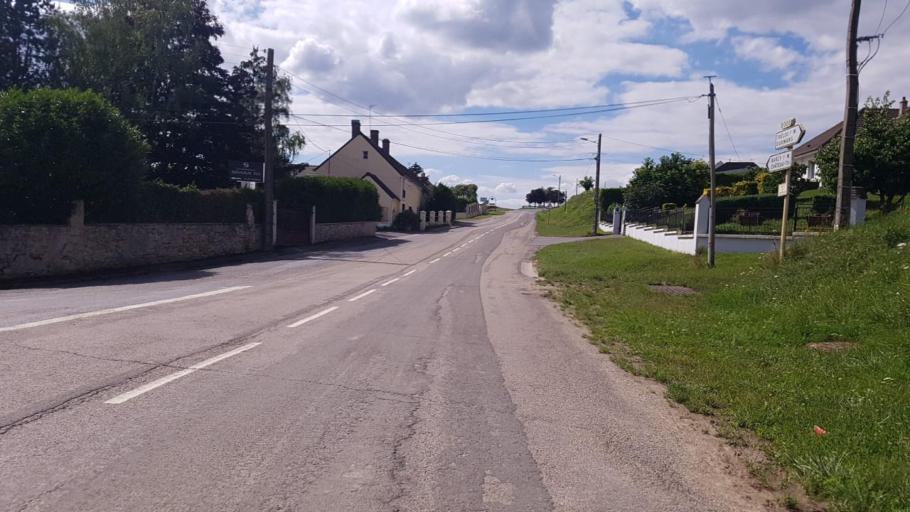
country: FR
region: Picardie
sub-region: Departement de l'Aisne
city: Crezancy
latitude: 49.0621
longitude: 3.5709
